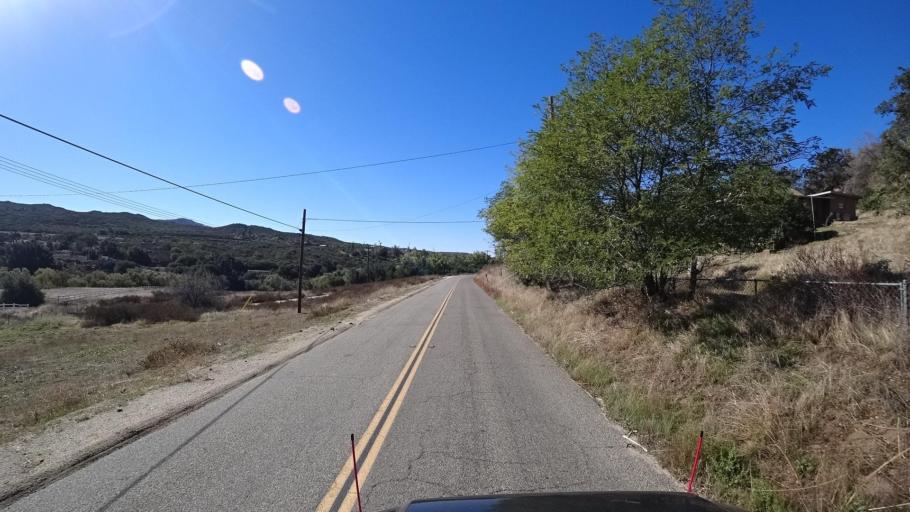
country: US
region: California
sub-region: San Diego County
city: Alpine
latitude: 32.8422
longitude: -116.7114
